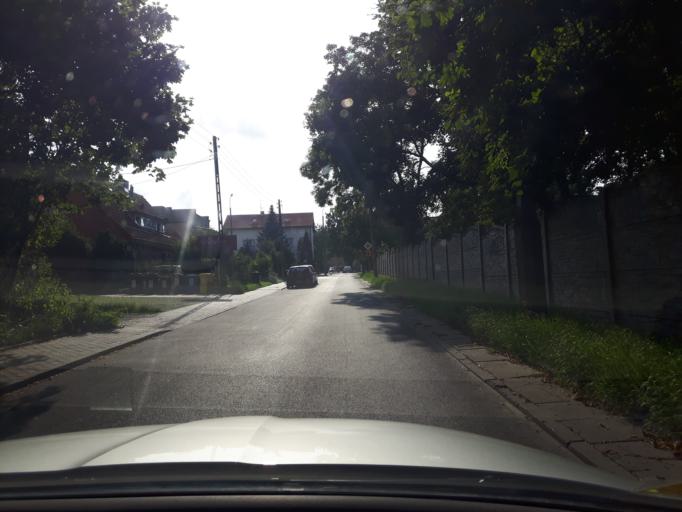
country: PL
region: Pomeranian Voivodeship
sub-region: Gdansk
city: Gdansk
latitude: 54.3437
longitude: 18.6296
